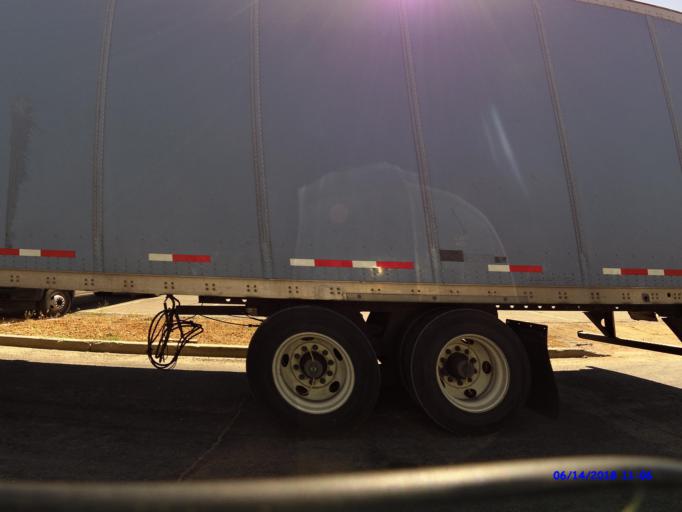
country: US
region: Utah
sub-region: Weber County
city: Ogden
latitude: 41.2143
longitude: -112.0032
